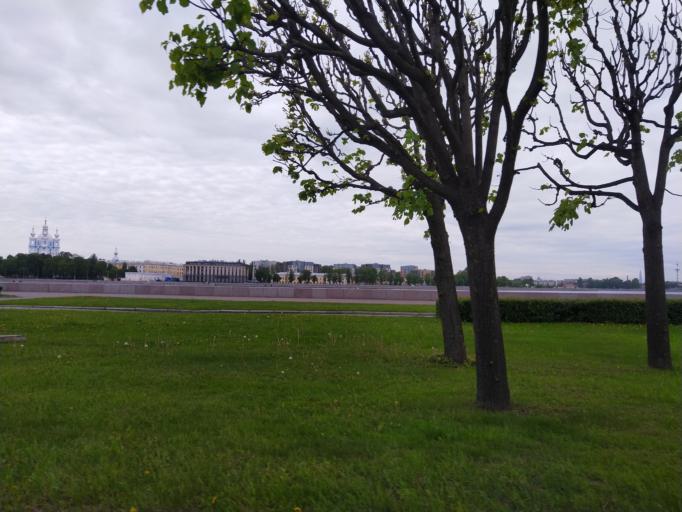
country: RU
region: Leningrad
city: Finlyandskiy
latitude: 59.9543
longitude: 30.4073
